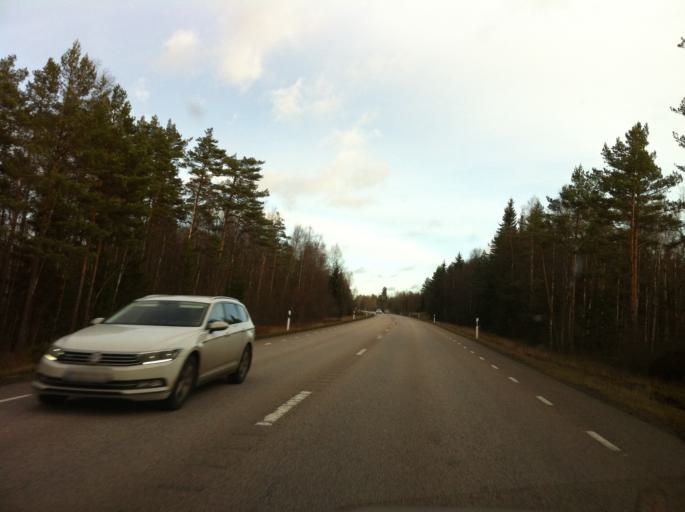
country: SE
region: Kronoberg
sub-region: Uppvidinge Kommun
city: Aseda
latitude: 57.1570
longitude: 15.3239
